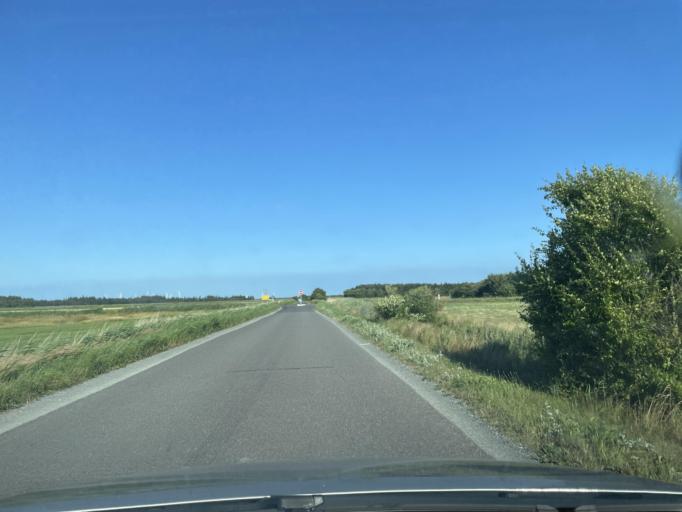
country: DE
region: Schleswig-Holstein
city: Aventoft
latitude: 54.8795
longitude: 8.8064
